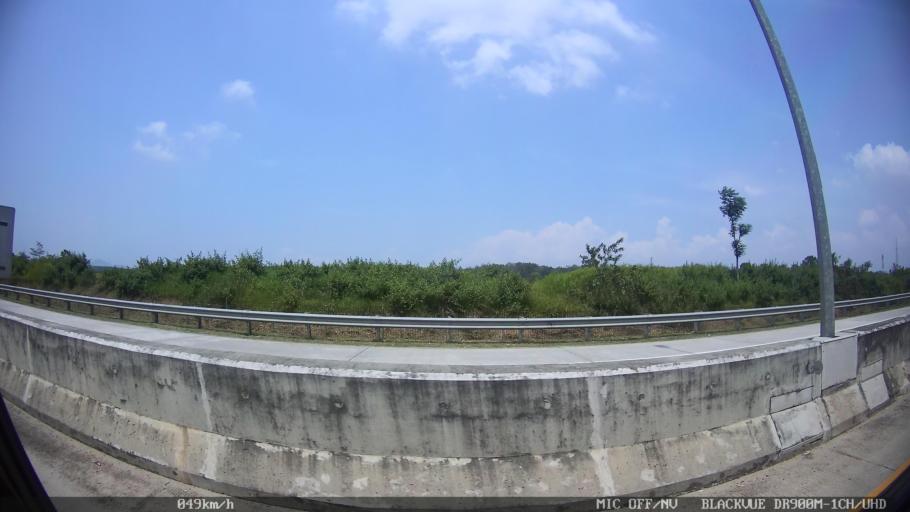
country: ID
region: Lampung
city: Kedaton
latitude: -5.3557
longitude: 105.3269
